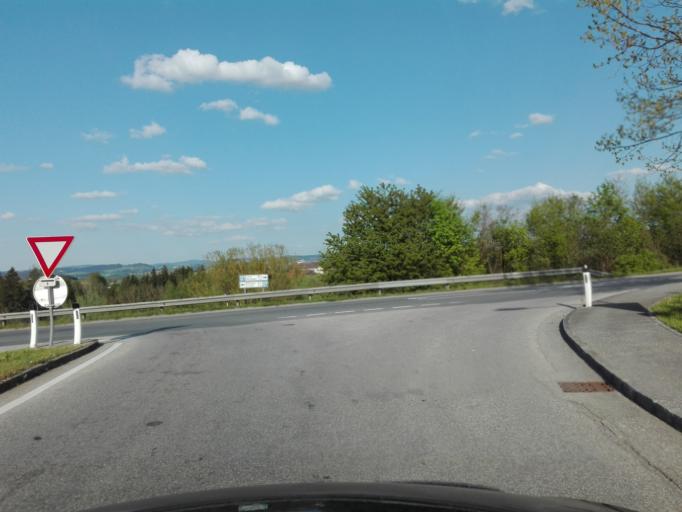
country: AT
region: Upper Austria
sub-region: Politischer Bezirk Rohrbach
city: Kleinzell im Muehlkreis
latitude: 48.4911
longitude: 13.9706
